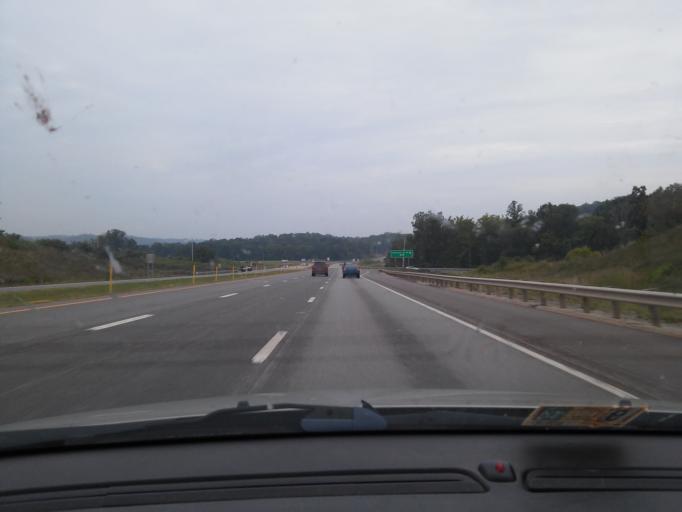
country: US
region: West Virginia
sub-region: Putnam County
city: Eleanor
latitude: 38.5494
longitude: -81.9825
